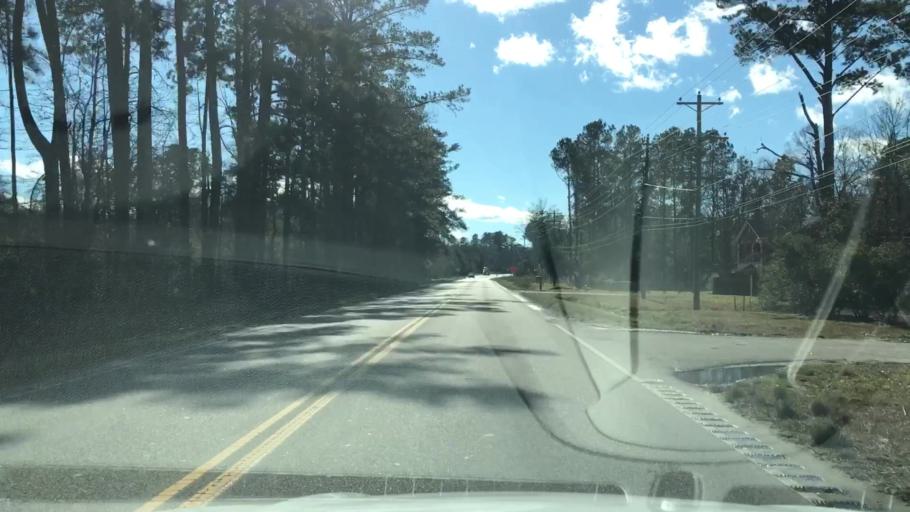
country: US
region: South Carolina
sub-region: Dorchester County
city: Summerville
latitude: 33.0877
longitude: -80.2008
